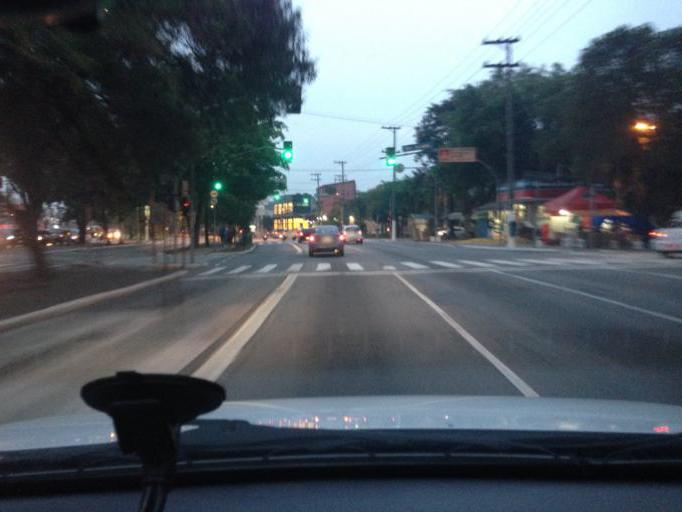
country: BR
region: Sao Paulo
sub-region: Sao Paulo
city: Sao Paulo
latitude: -23.4981
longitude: -46.7068
